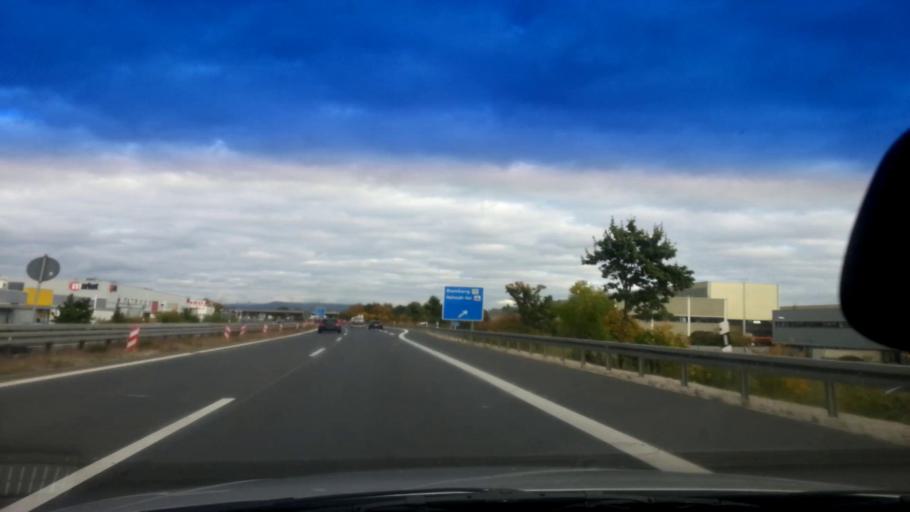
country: DE
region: Bavaria
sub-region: Upper Franconia
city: Hallstadt
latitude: 49.9231
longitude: 10.8943
